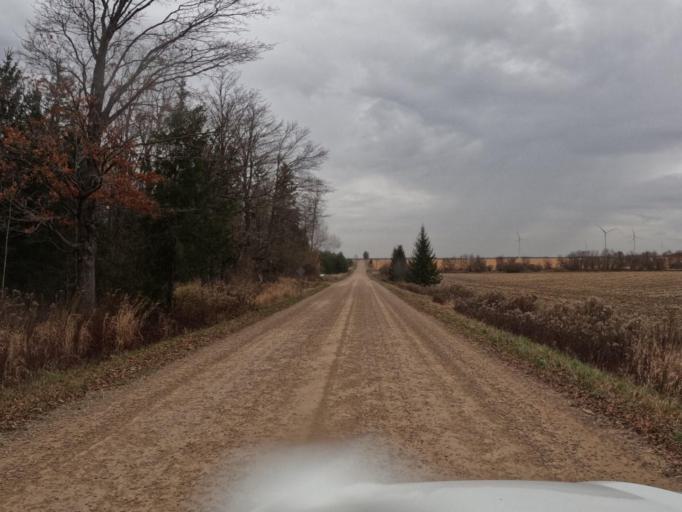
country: CA
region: Ontario
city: Shelburne
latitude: 43.8741
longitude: -80.3794
